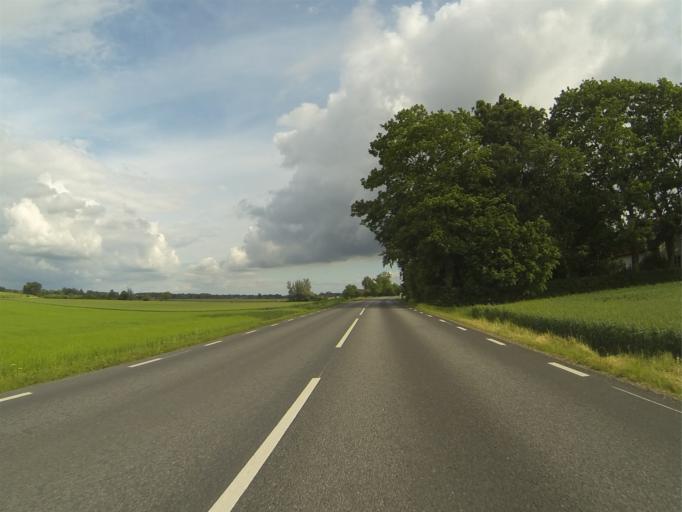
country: SE
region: Skane
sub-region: Eslovs Kommun
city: Eslov
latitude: 55.7553
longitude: 13.3208
